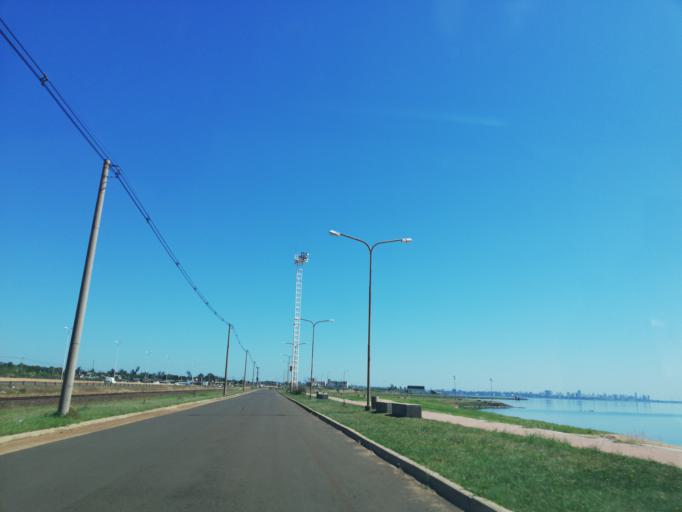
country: AR
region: Misiones
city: Garupa
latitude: -27.4313
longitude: -55.8656
